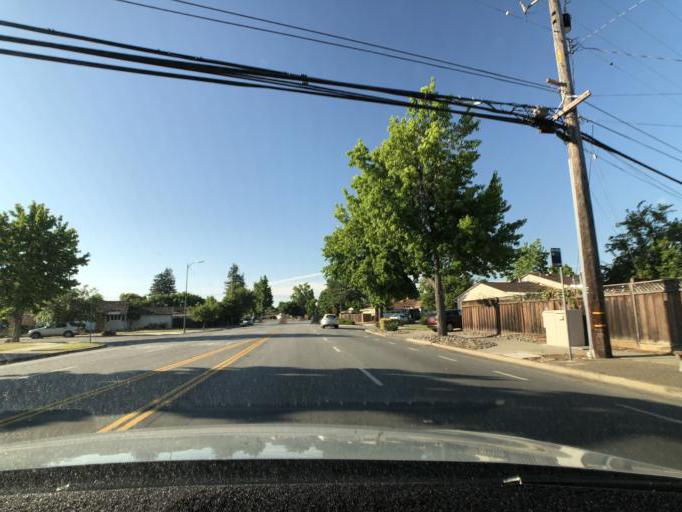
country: US
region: California
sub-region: Santa Clara County
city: Cambrian Park
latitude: 37.2718
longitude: -121.9208
